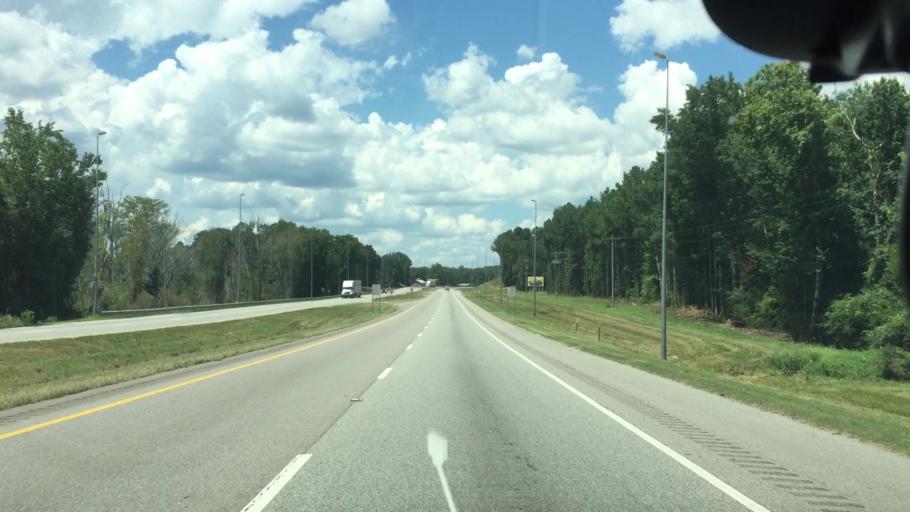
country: US
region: Alabama
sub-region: Pike County
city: Troy
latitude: 31.8177
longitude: -85.9930
